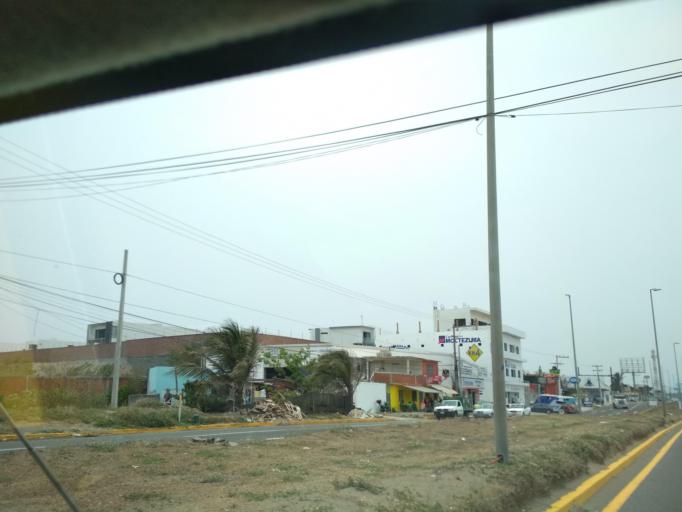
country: MX
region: Veracruz
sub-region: Alvarado
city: Playa de la Libertad
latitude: 19.0693
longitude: -96.0828
